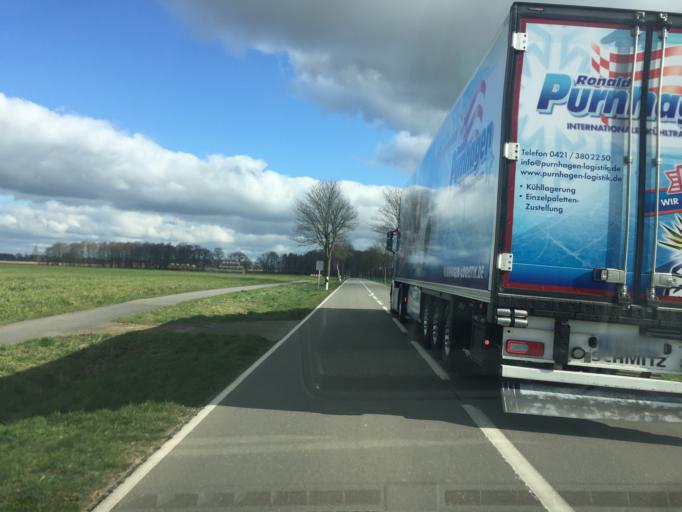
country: DE
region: Lower Saxony
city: Affinghausen
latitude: 52.7903
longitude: 8.8913
